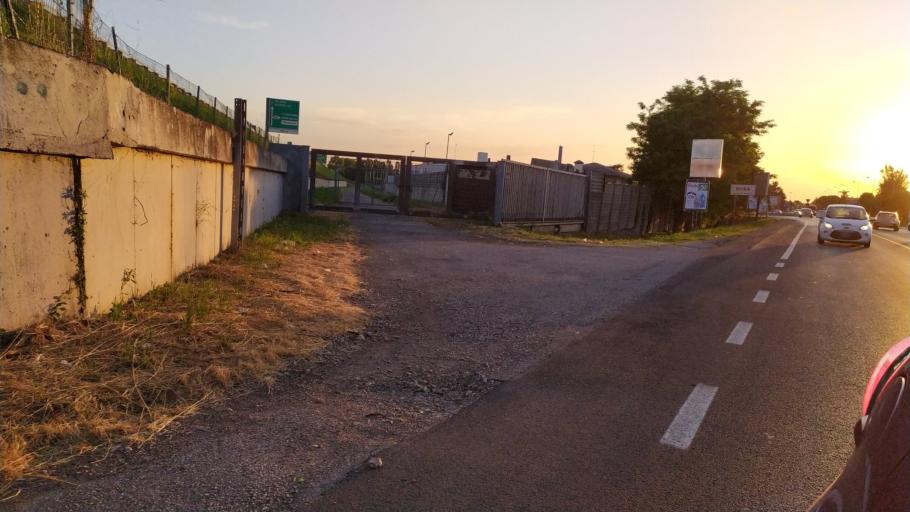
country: IT
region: Veneto
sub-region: Provincia di Padova
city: San Vito
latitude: 45.4249
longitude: 11.9692
